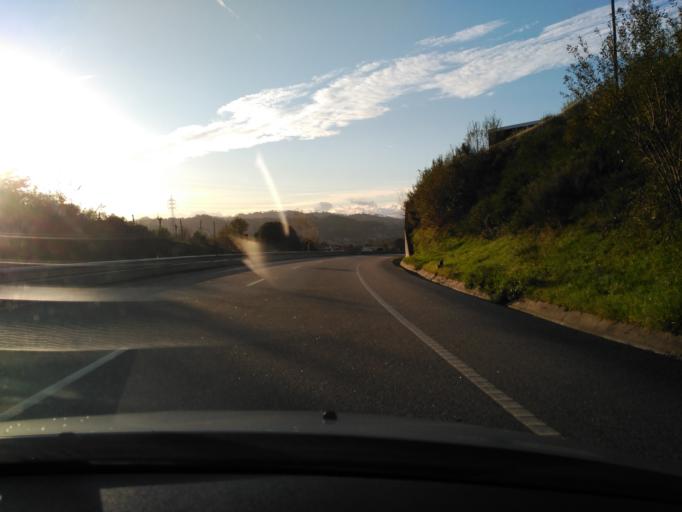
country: PT
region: Braga
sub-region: Fafe
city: Aroes
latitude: 41.4554
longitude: -8.2184
